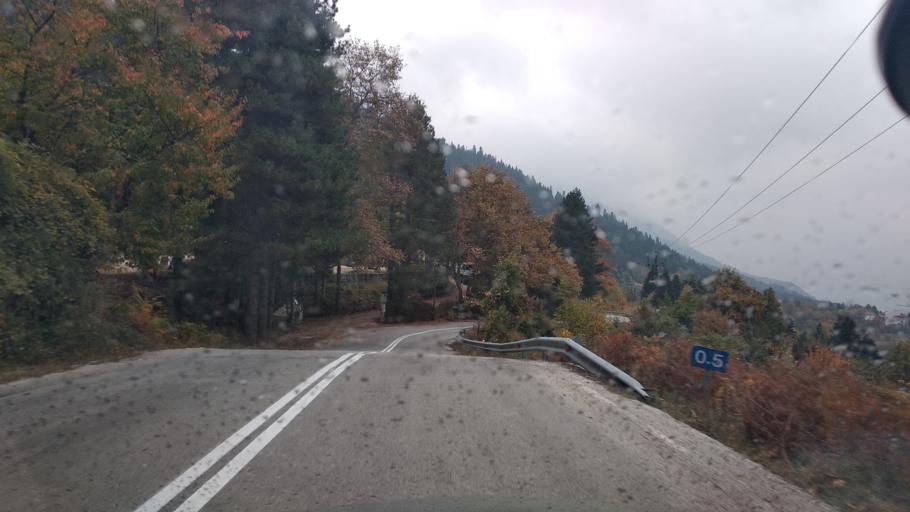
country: GR
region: Thessaly
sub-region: Trikala
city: Pyli
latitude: 39.5131
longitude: 21.5295
